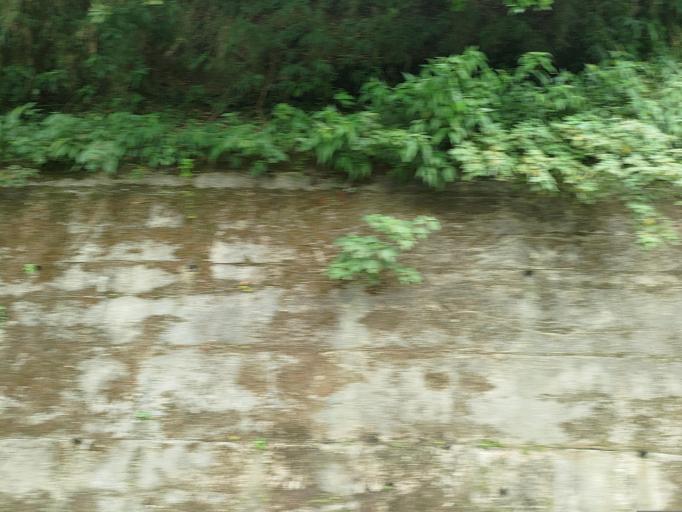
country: TW
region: Taiwan
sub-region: Miaoli
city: Miaoli
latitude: 24.6000
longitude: 121.0294
